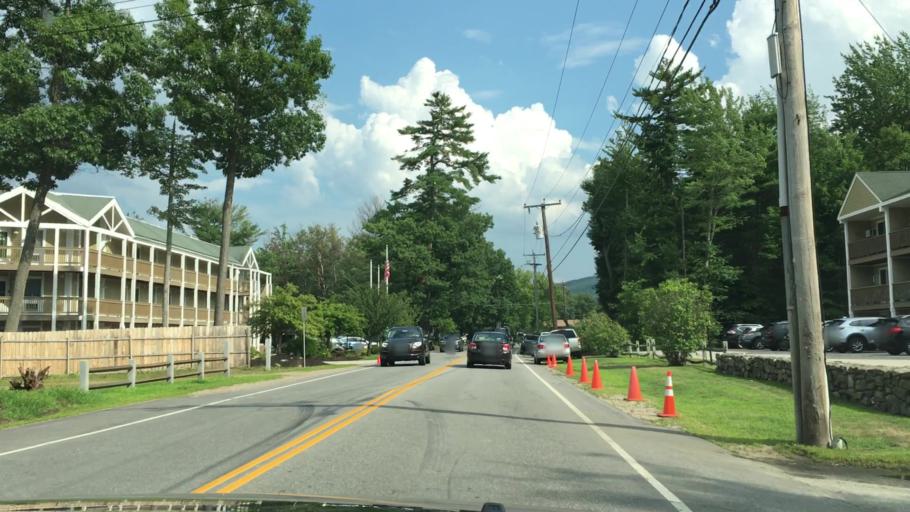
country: US
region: New Hampshire
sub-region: Belknap County
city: Gilford
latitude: 43.5817
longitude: -71.4104
